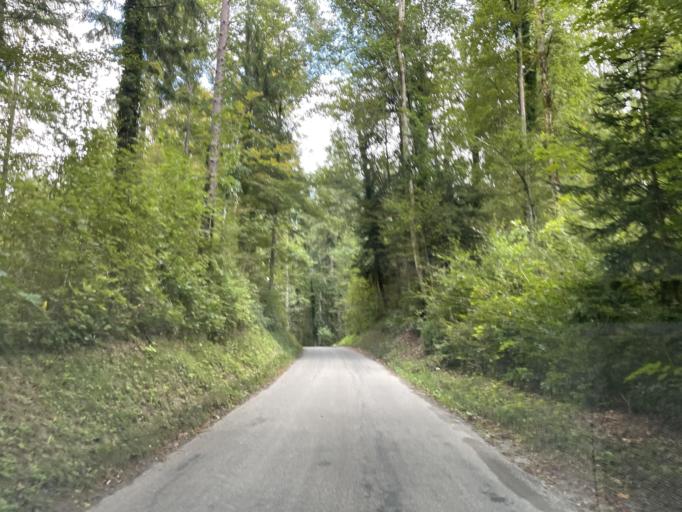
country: CH
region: Zurich
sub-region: Bezirk Winterthur
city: Seen (Kreis 3) / Waldegg
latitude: 47.4753
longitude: 8.7530
